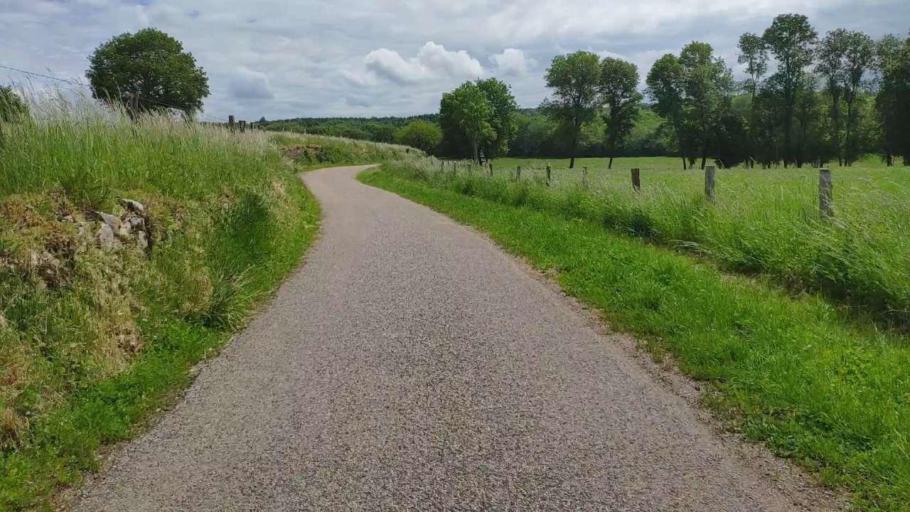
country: FR
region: Franche-Comte
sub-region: Departement du Jura
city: Poligny
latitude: 46.7557
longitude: 5.6410
